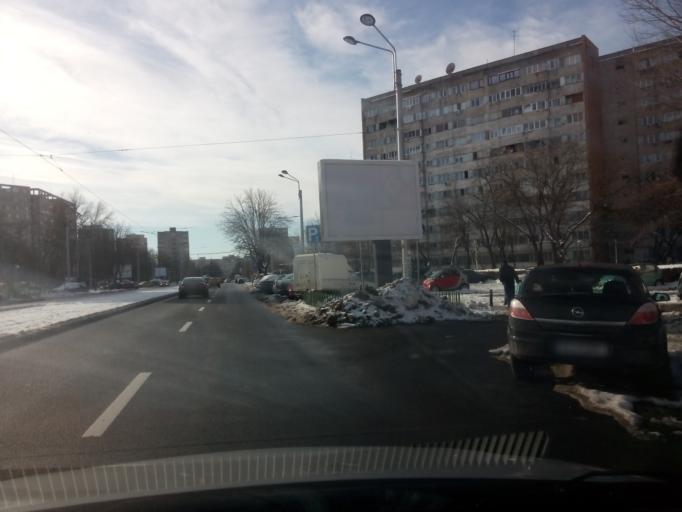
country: RO
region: Ilfov
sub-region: Comuna Popesti-Leordeni
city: Popesti-Leordeni
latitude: 44.4202
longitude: 26.1479
